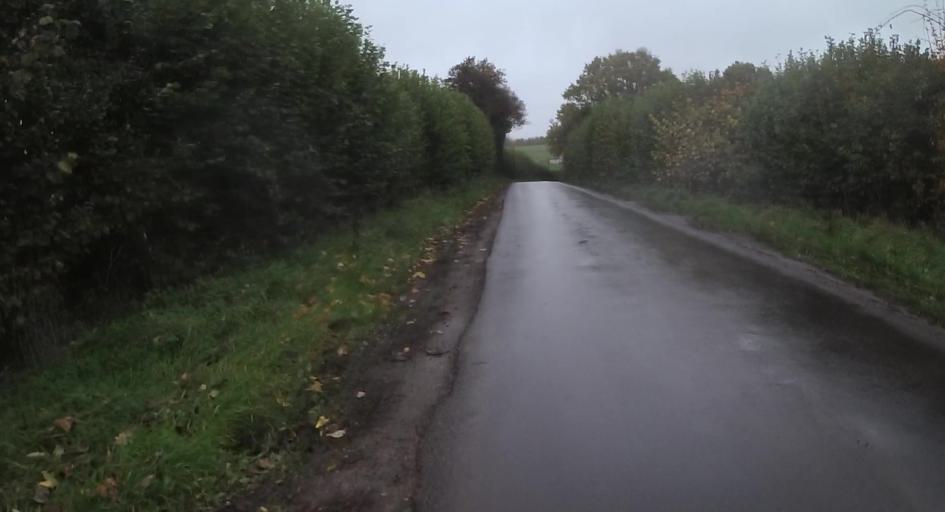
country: GB
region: England
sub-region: Surrey
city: Farnham
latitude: 51.2108
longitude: -0.8553
